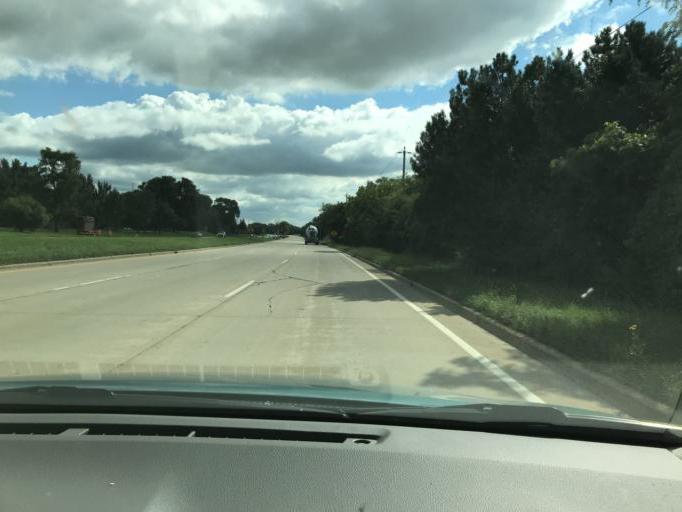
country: US
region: Wisconsin
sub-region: Kenosha County
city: Pleasant Prairie
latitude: 42.5557
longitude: -87.8913
